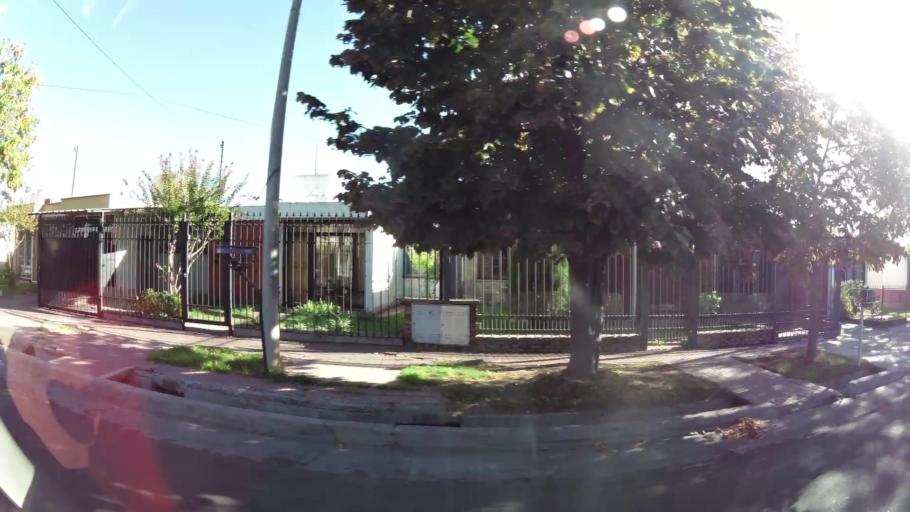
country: AR
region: Mendoza
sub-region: Departamento de Godoy Cruz
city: Godoy Cruz
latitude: -32.9307
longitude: -68.8364
